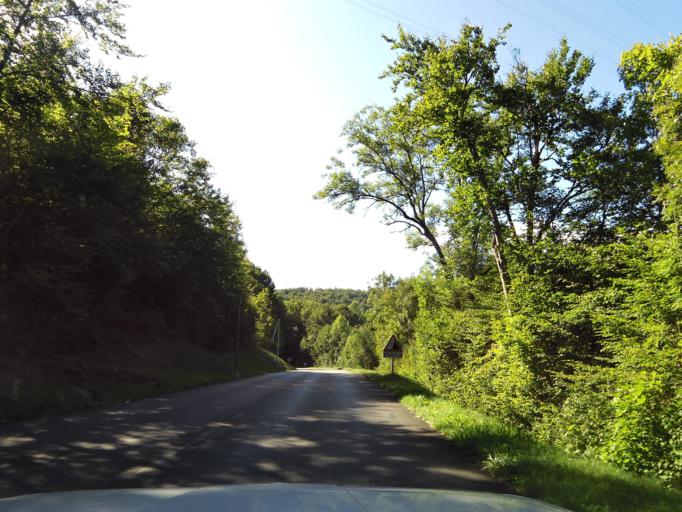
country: FR
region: Rhone-Alpes
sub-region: Departement de l'Ain
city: Hauteville-Lompnes
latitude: 45.9655
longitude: 5.5709
